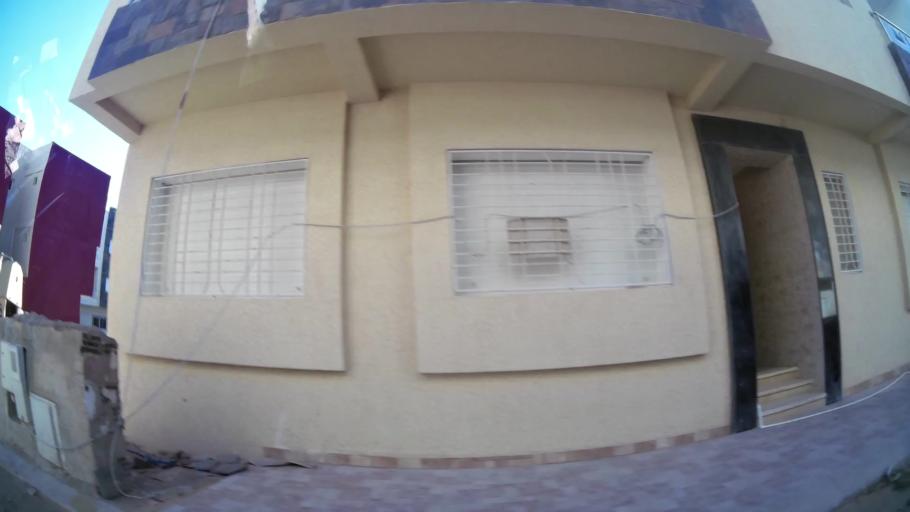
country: MA
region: Oriental
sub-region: Berkane-Taourirt
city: Madagh
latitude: 35.0917
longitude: -2.2588
